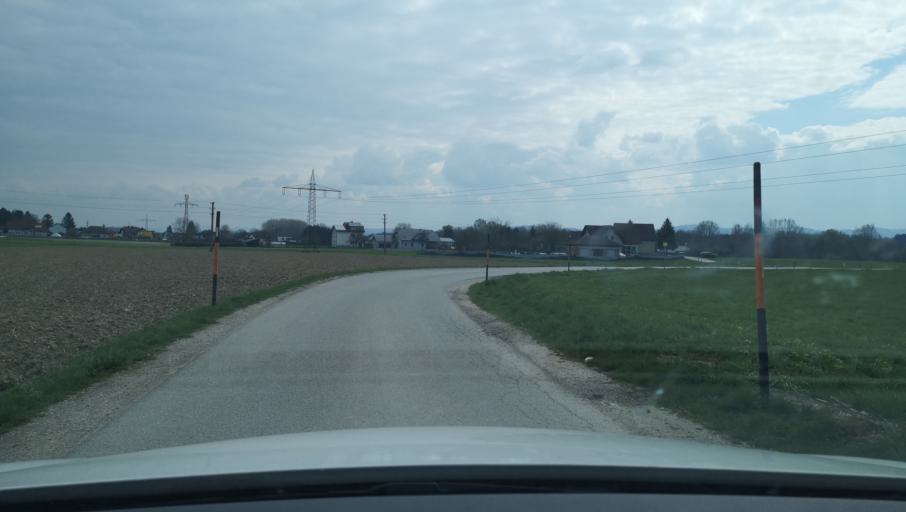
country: AT
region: Lower Austria
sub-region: Politischer Bezirk Amstetten
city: Amstetten
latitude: 48.1154
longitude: 14.8879
